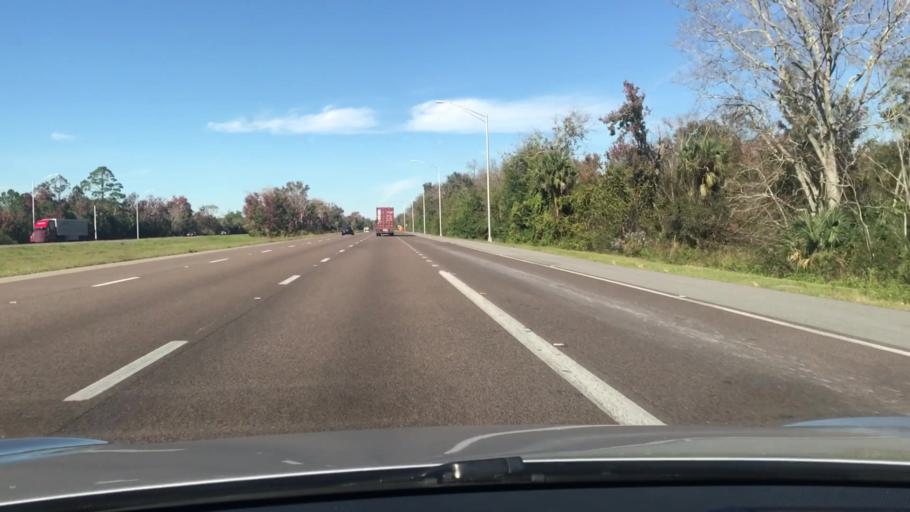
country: US
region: Florida
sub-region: Volusia County
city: Edgewater
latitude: 28.9550
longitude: -80.9523
